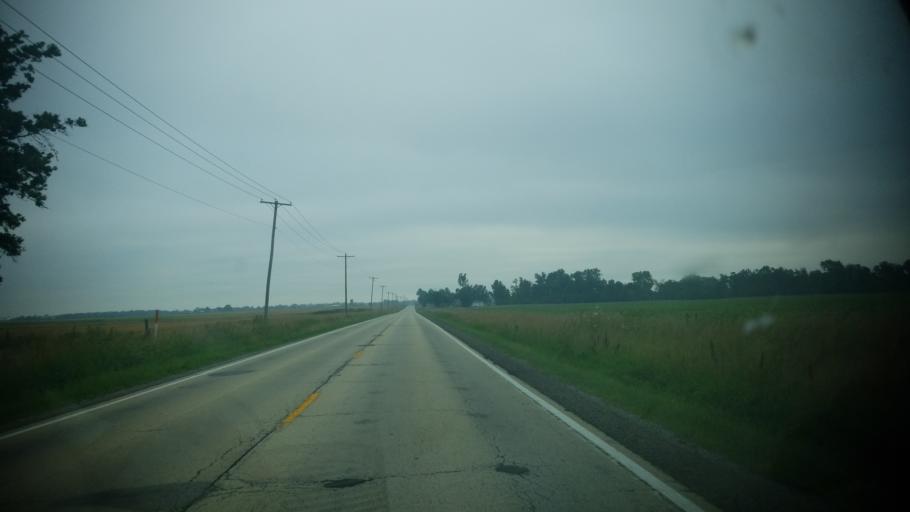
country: US
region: Illinois
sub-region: Clay County
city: Flora
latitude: 38.6512
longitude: -88.4384
